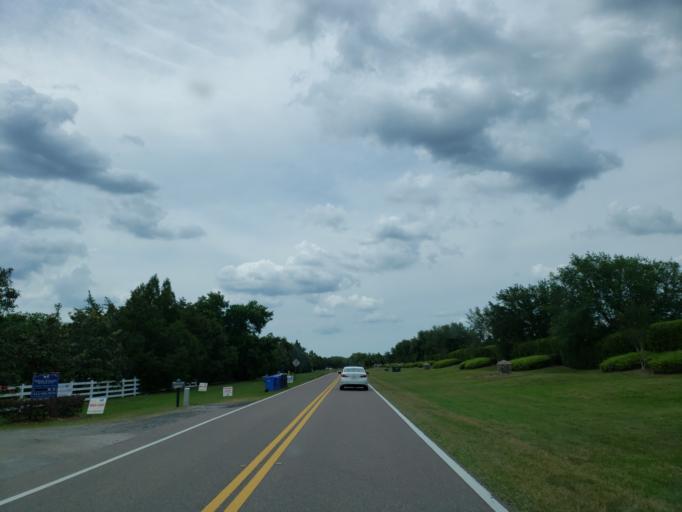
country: US
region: Florida
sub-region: Hillsborough County
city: Keystone
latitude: 28.1193
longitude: -82.6096
